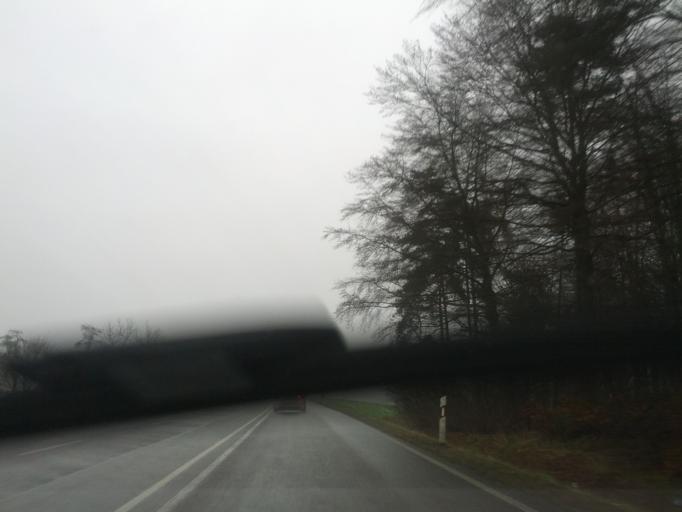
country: DE
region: Thuringia
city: Gerstungen
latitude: 51.0189
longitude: 10.0530
